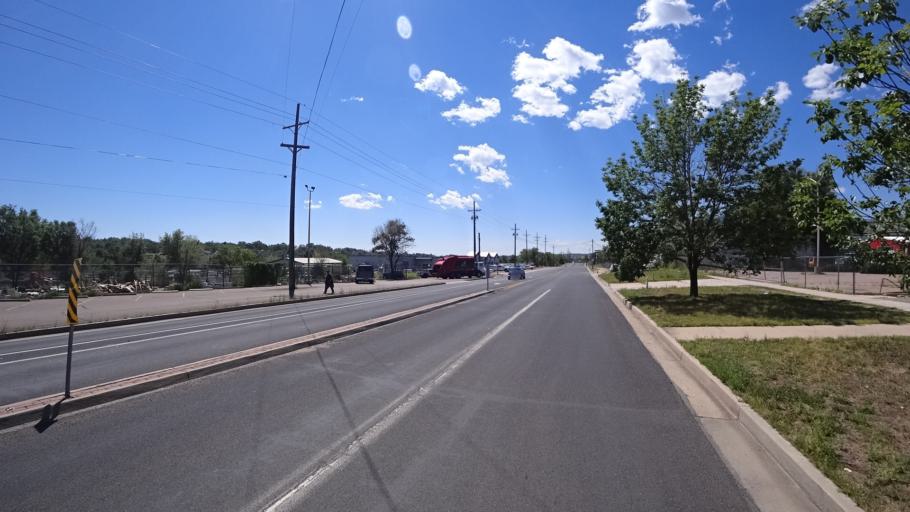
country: US
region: Colorado
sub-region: El Paso County
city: Colorado Springs
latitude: 38.8266
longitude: -104.8185
